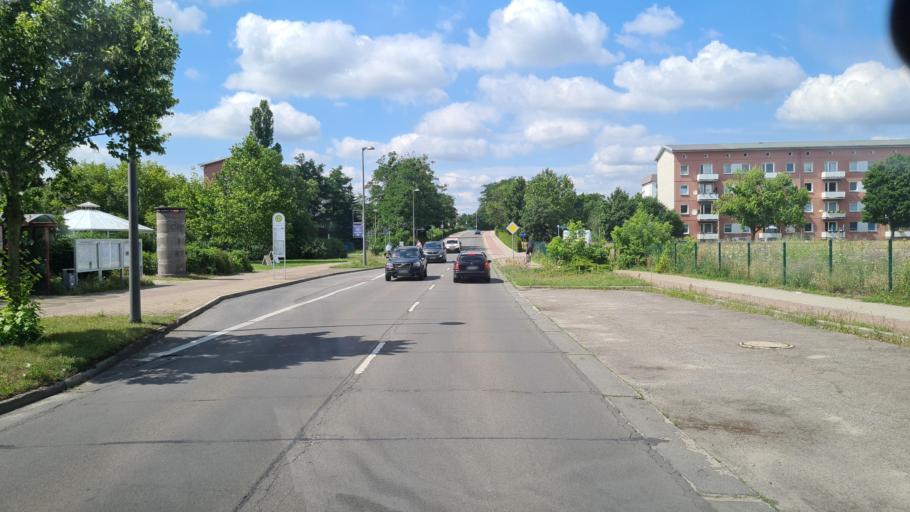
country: DE
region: Brandenburg
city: Senftenberg
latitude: 51.5152
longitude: 13.9840
